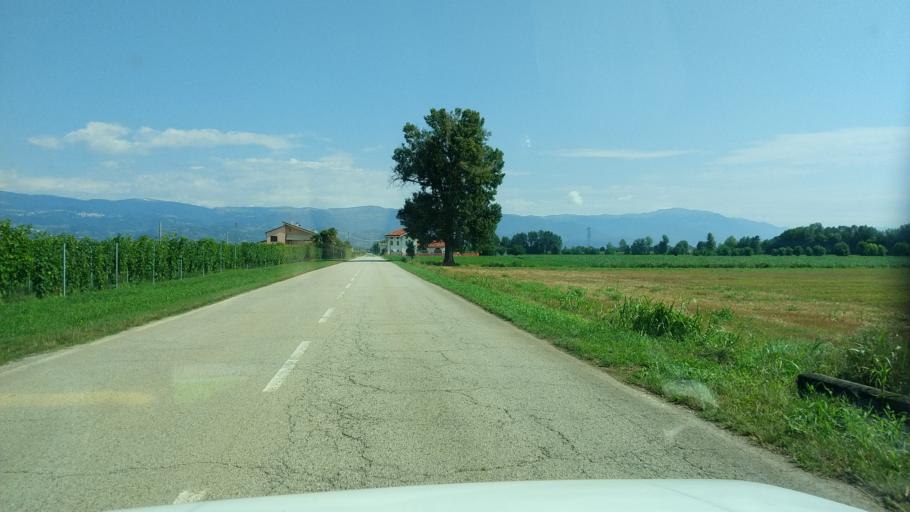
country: IT
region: Veneto
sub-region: Provincia di Vicenza
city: Sandrigo
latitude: 45.6697
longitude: 11.6076
